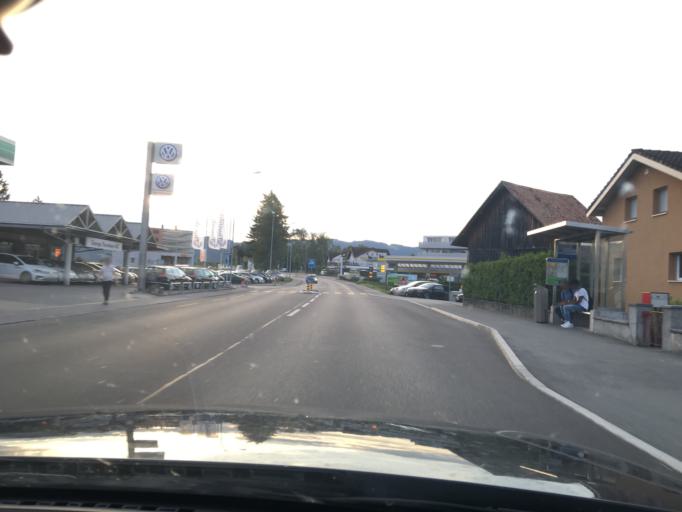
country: CH
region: Saint Gallen
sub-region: Wahlkreis Rheintal
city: Diepoldsau
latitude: 47.3885
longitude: 9.6518
